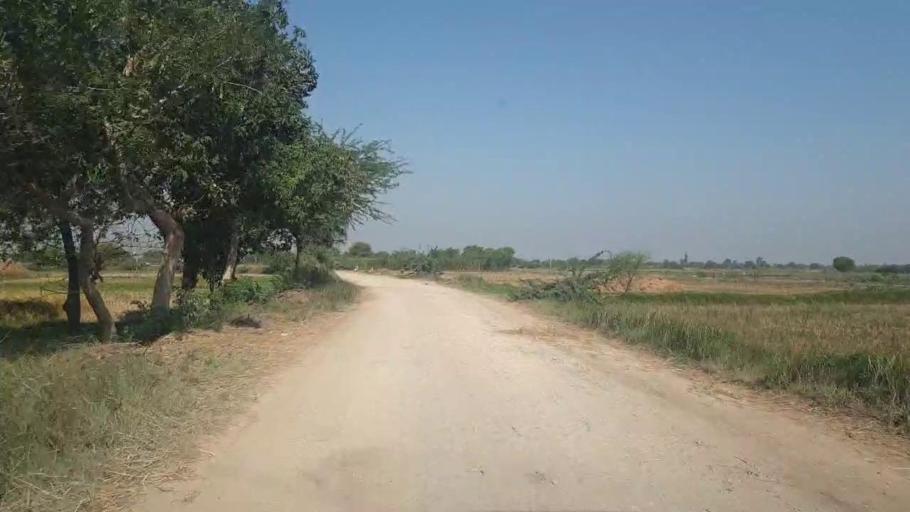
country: PK
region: Sindh
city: Badin
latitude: 24.6736
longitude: 68.8585
